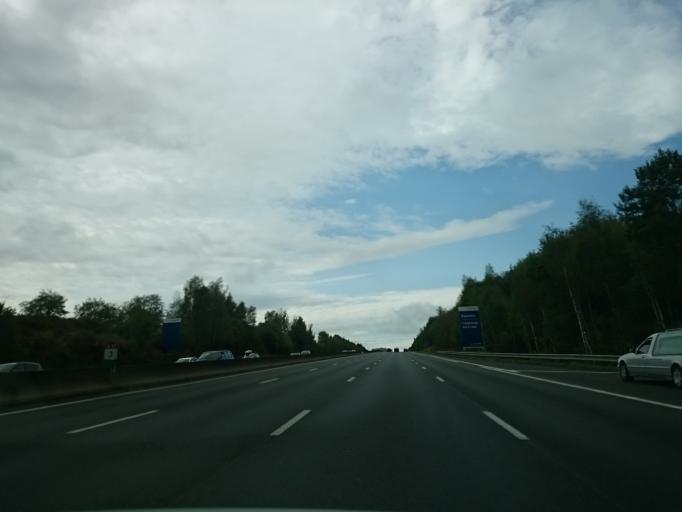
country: FR
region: Ile-de-France
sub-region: Departement de l'Essonne
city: Les Ulis
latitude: 48.6503
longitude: 2.1702
